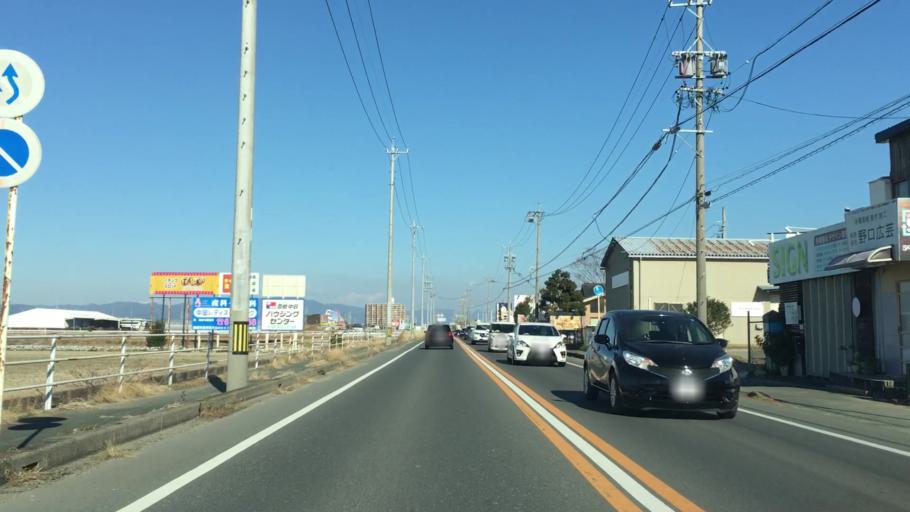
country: JP
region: Aichi
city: Toyohashi
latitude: 34.7306
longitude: 137.3586
